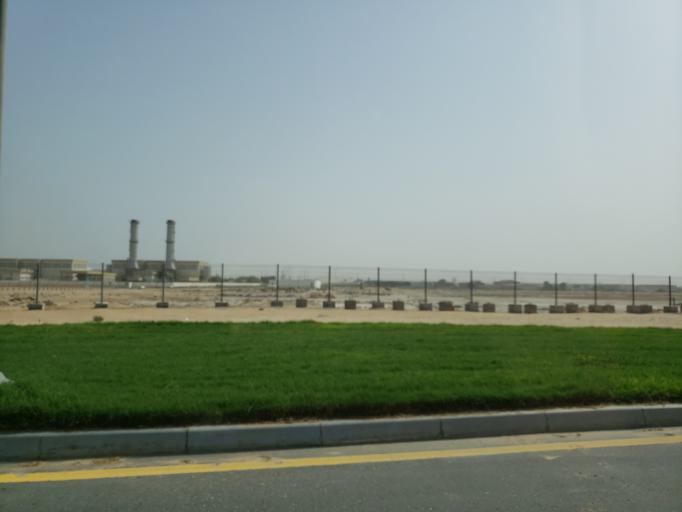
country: AE
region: Ajman
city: Ajman
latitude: 25.4399
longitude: 55.4765
